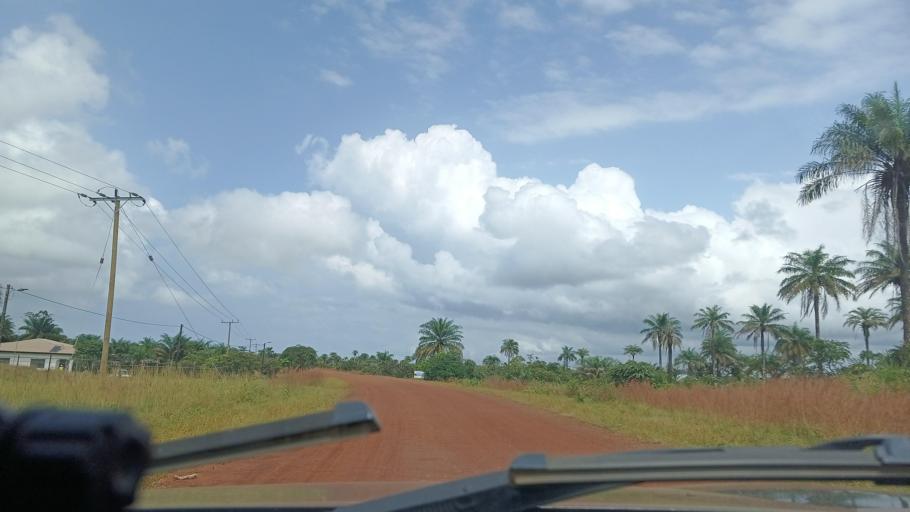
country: LR
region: Grand Cape Mount
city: Robertsport
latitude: 6.7464
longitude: -11.3396
